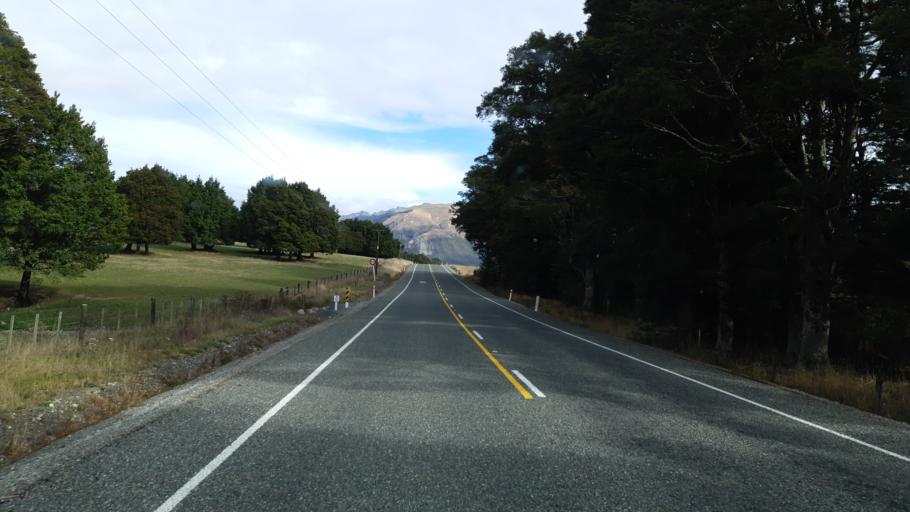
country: NZ
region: Tasman
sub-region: Tasman District
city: Wakefield
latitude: -41.7903
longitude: 172.8823
